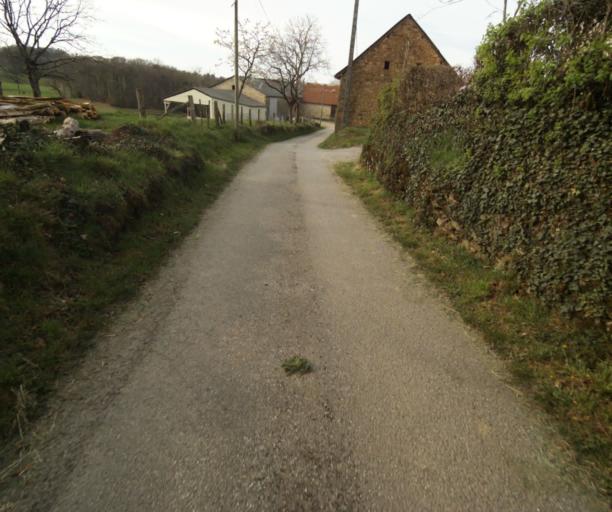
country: FR
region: Limousin
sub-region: Departement de la Correze
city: Chamboulive
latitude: 45.4491
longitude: 1.7791
